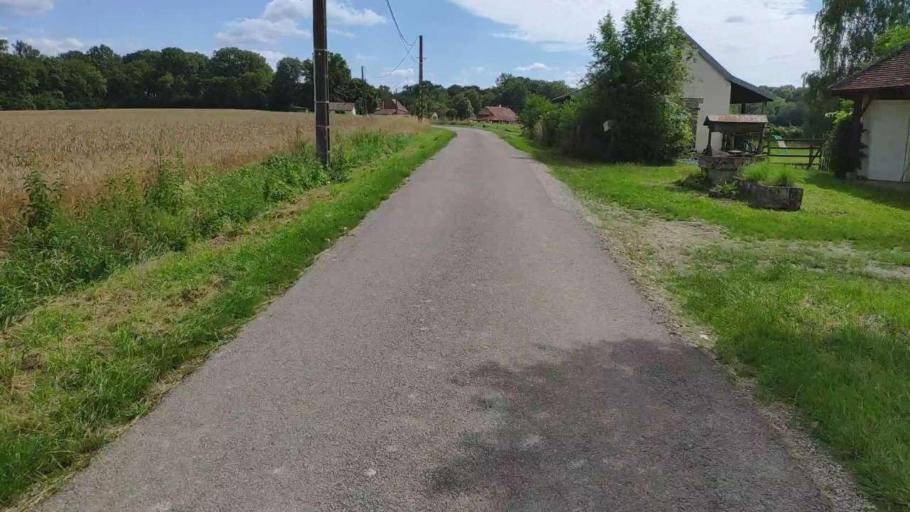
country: FR
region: Franche-Comte
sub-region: Departement du Jura
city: Bletterans
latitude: 46.8102
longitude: 5.4269
